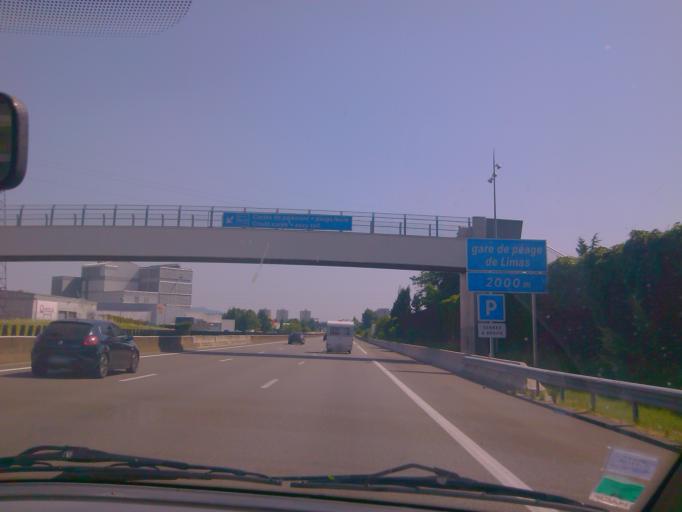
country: FR
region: Rhone-Alpes
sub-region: Departement du Rhone
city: Villefranche-sur-Saone
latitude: 45.9912
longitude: 4.7371
